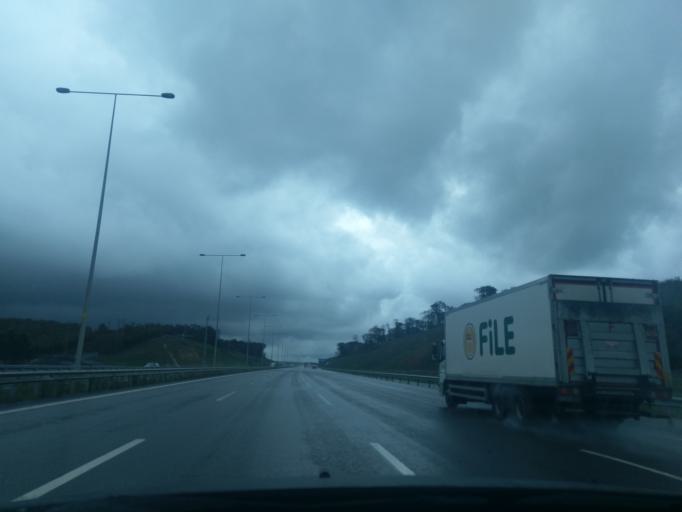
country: TR
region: Istanbul
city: Kemerburgaz
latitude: 41.2354
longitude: 28.8884
